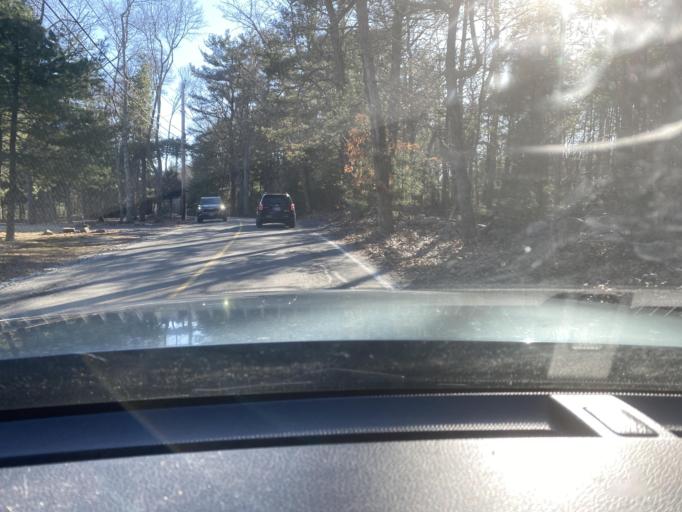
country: US
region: Massachusetts
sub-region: Middlesex County
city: Sherborn
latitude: 42.2239
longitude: -71.3719
